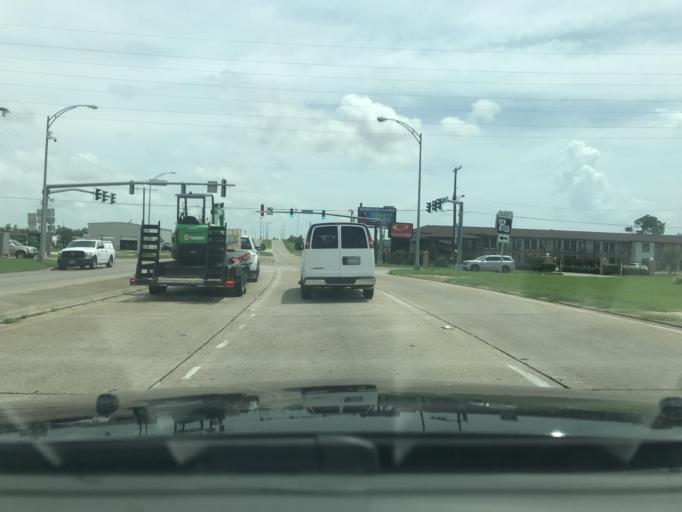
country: US
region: Louisiana
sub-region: Calcasieu Parish
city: Lake Charles
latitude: 30.2428
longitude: -93.1806
